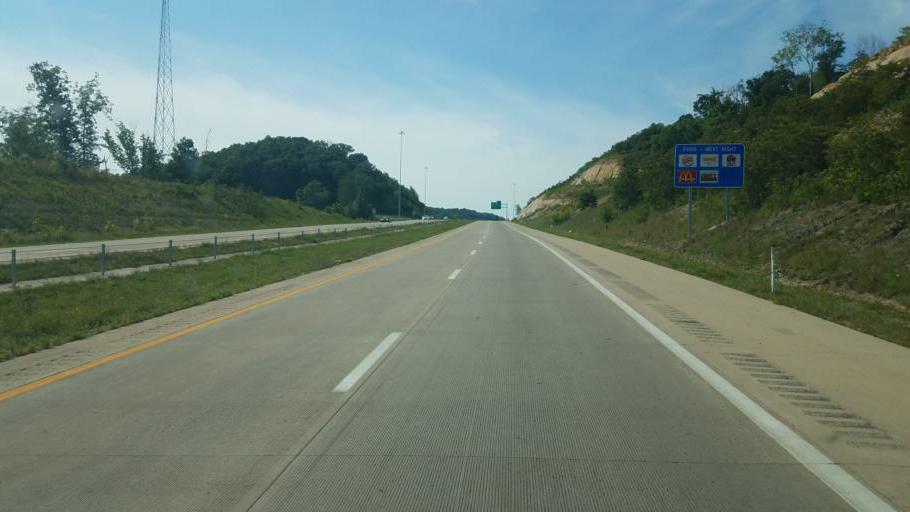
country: US
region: Ohio
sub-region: Athens County
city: Nelsonville
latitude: 39.4353
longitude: -82.1995
